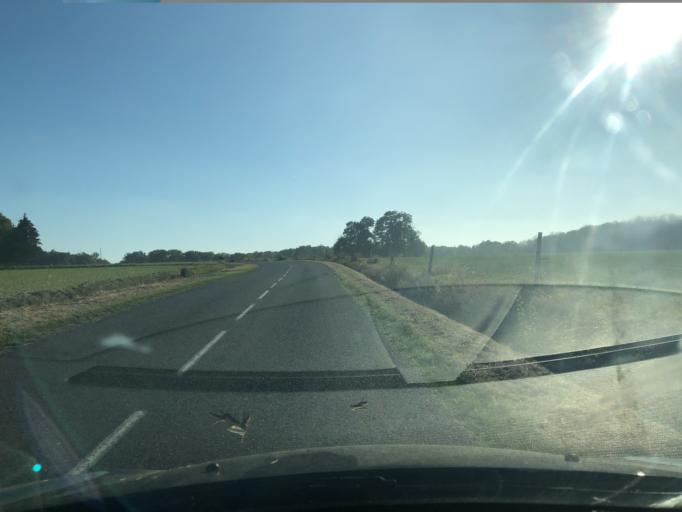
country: FR
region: Centre
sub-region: Departement d'Indre-et-Loire
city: Neuvy-le-Roi
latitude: 47.5942
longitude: 0.5956
